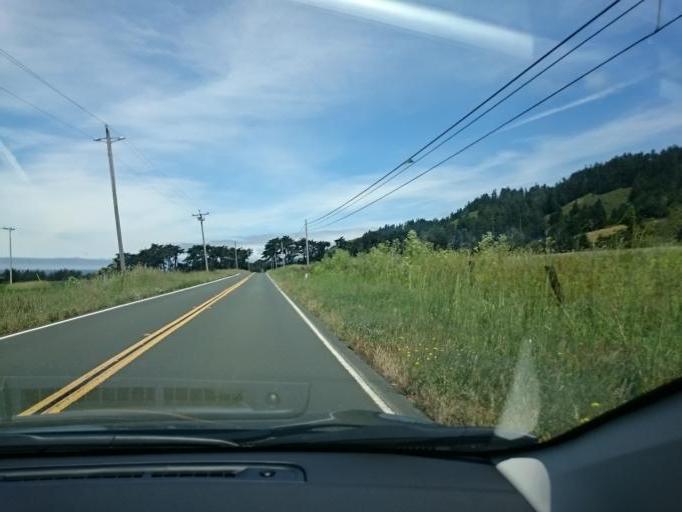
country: US
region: California
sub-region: Mendocino County
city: Boonville
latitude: 39.0848
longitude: -123.6985
